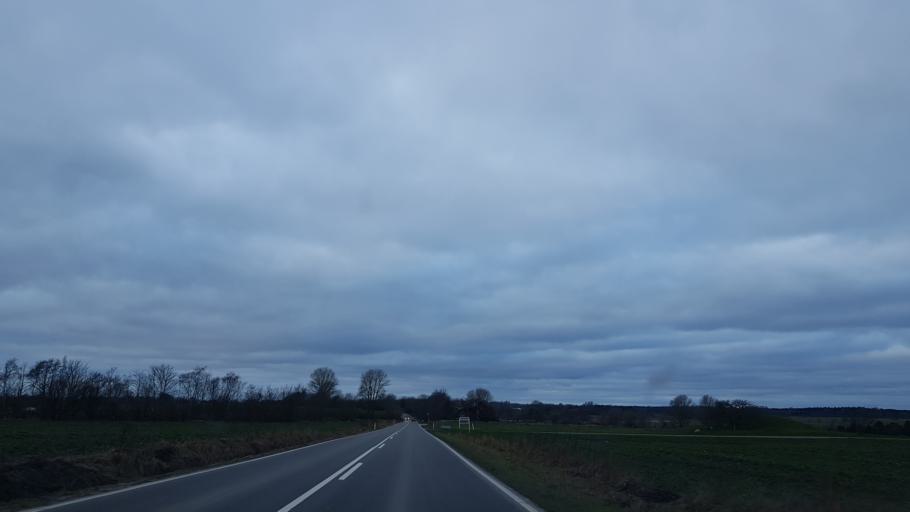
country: DK
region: Zealand
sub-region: Odsherred Kommune
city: Hojby
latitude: 55.9322
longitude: 11.6019
